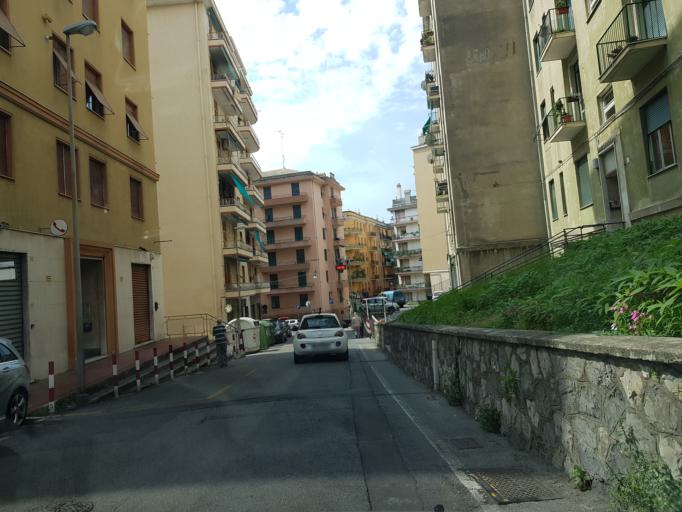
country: IT
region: Liguria
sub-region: Provincia di Genova
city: San Teodoro
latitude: 44.4284
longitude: 8.8465
